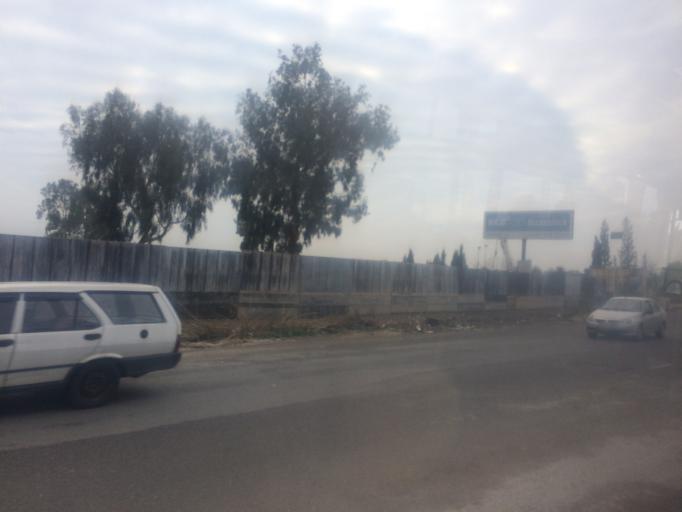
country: TR
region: Izmir
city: Karsiyaka
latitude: 38.4936
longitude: 27.0477
